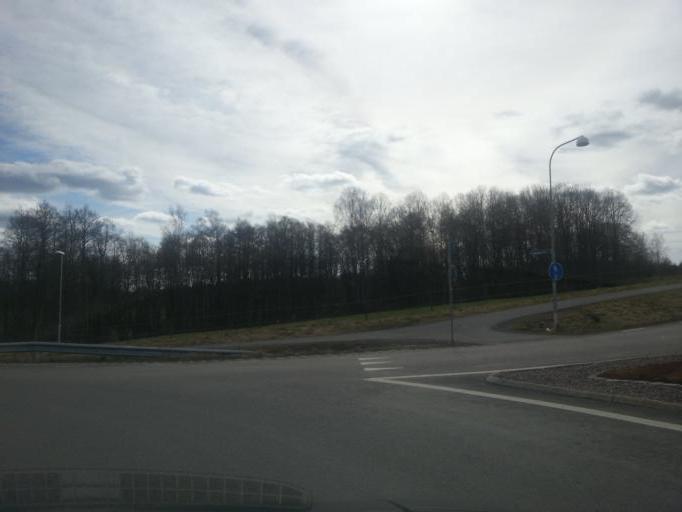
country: SE
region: Joenkoeping
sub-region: Jonkopings Kommun
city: Jonkoping
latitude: 57.7904
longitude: 14.1183
